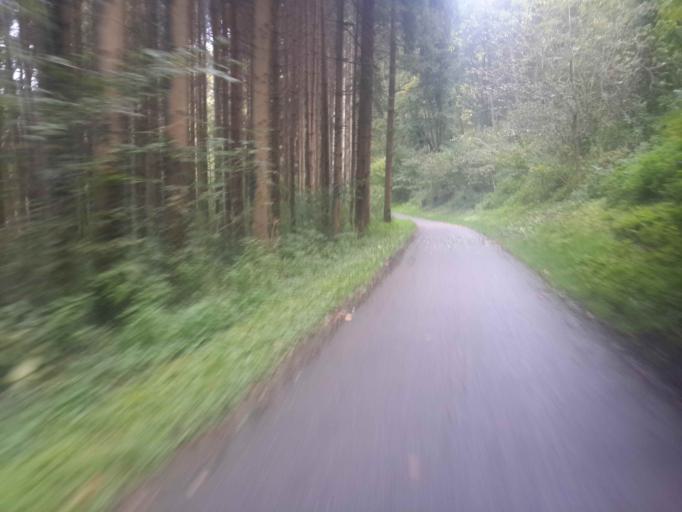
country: DE
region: Baden-Wuerttemberg
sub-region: Regierungsbezirk Stuttgart
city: Widdern
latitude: 49.3021
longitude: 9.4319
